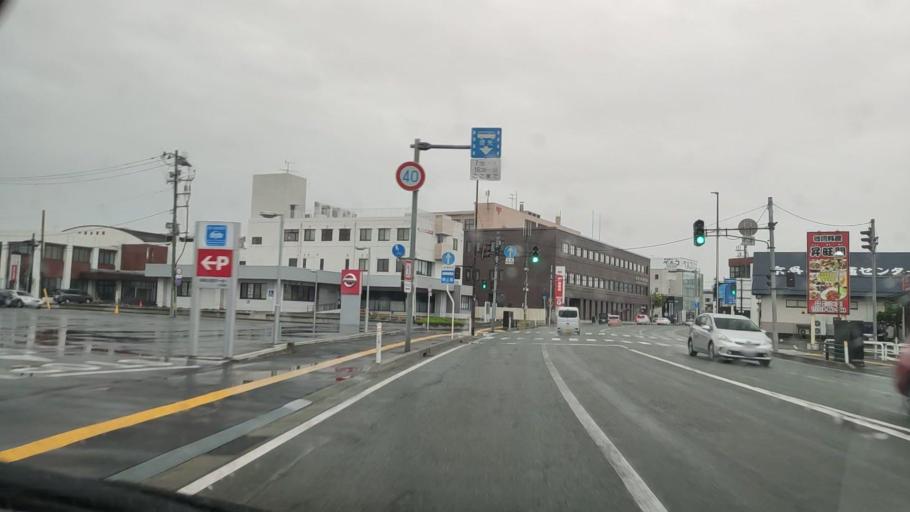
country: JP
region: Akita
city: Akita Shi
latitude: 39.7245
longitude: 140.1084
